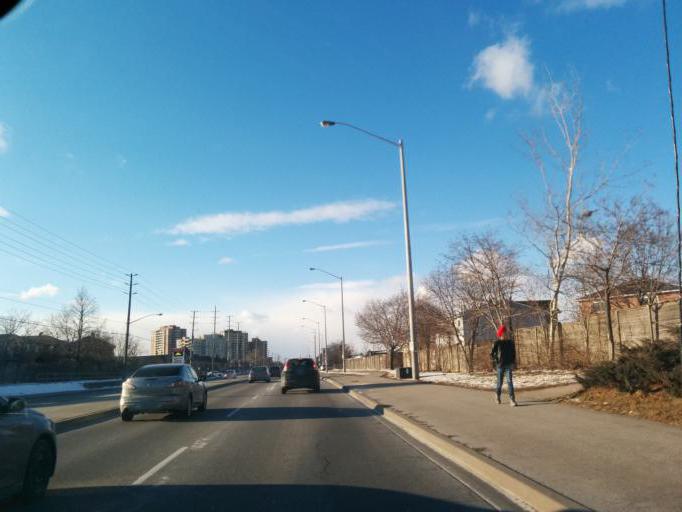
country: CA
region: Ontario
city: Brampton
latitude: 43.6491
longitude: -79.7335
